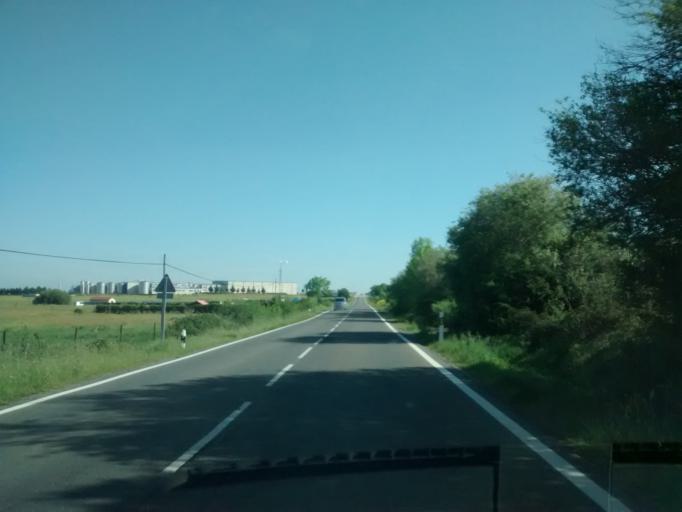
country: ES
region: Castille and Leon
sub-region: Provincia de Segovia
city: Trescasas
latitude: 40.9449
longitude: -4.0340
